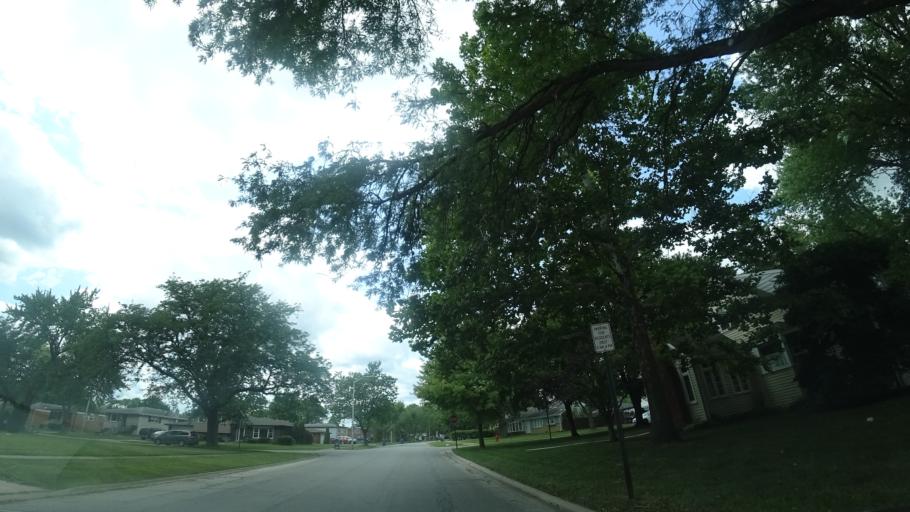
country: US
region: Illinois
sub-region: Cook County
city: Alsip
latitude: 41.6802
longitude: -87.7254
